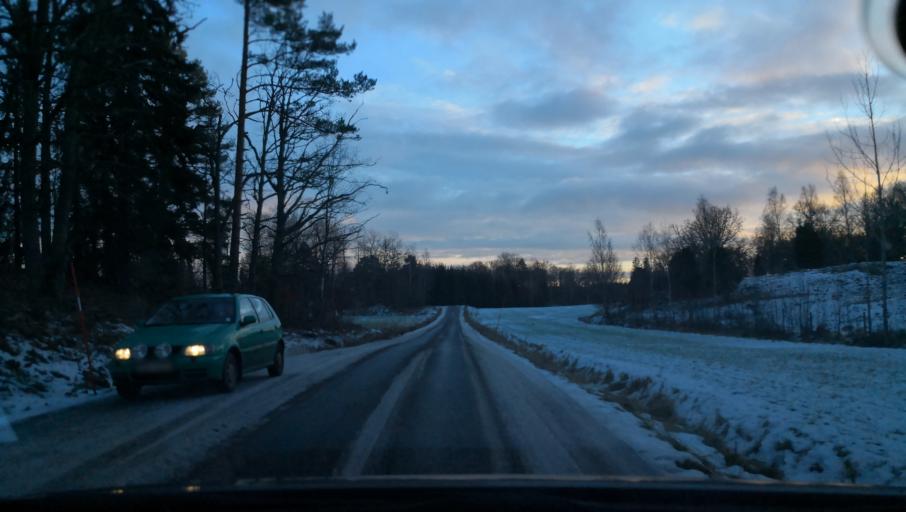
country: SE
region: Soedermanland
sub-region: Flens Kommun
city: Halleforsnas
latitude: 59.2285
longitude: 16.3361
